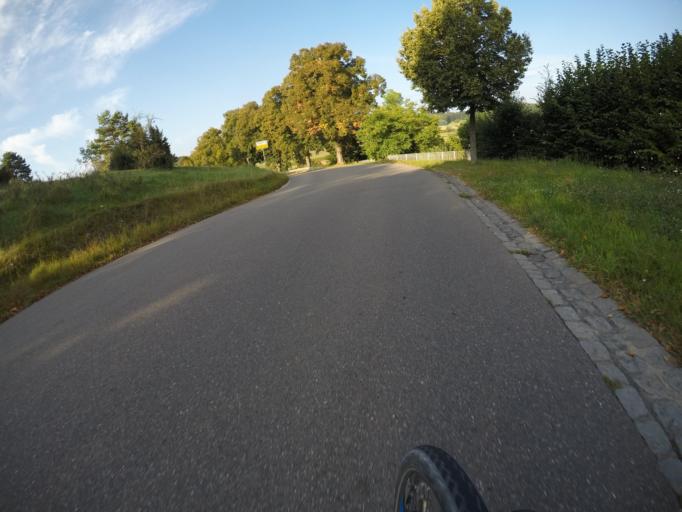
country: DE
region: Baden-Wuerttemberg
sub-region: Regierungsbezirk Stuttgart
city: Herbrechtingen
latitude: 48.6216
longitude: 10.1619
